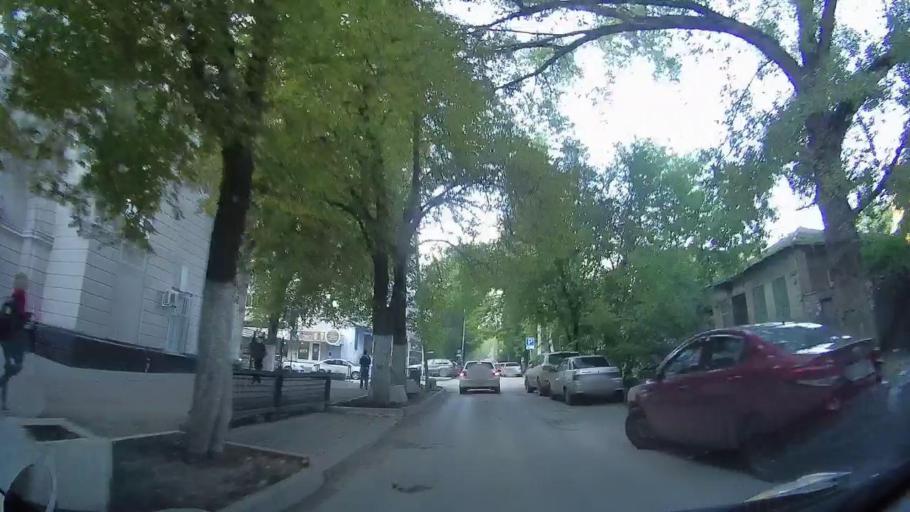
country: RU
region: Rostov
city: Rostov-na-Donu
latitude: 47.2302
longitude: 39.7092
